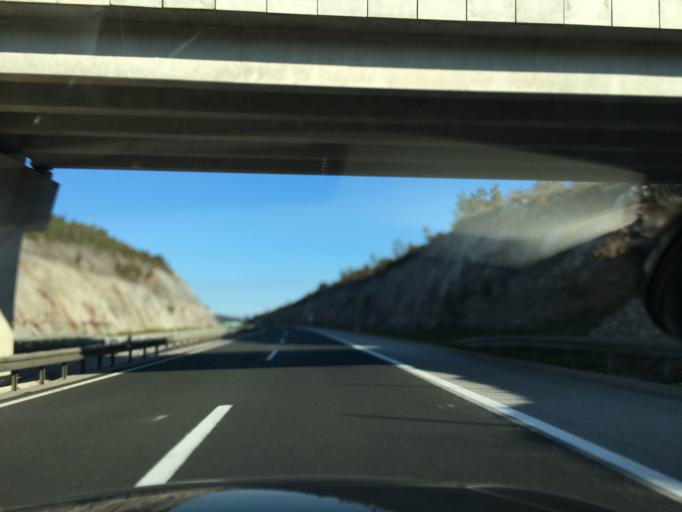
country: HR
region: Licko-Senjska
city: Otocac
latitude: 44.7430
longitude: 15.3782
